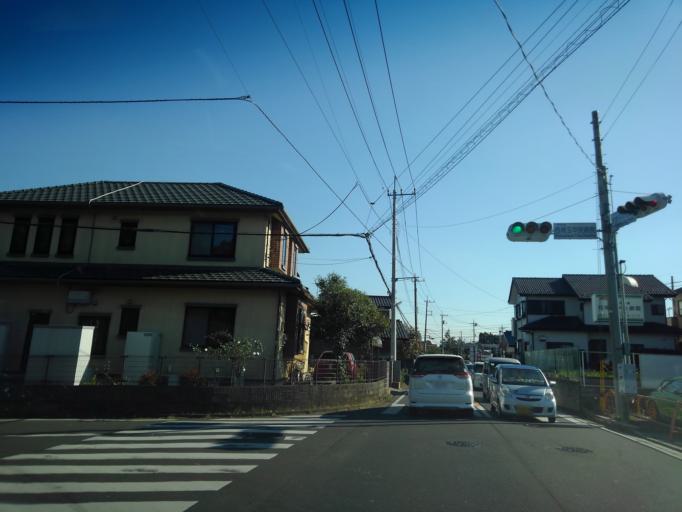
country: JP
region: Saitama
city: Tokorozawa
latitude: 35.8002
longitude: 139.4211
